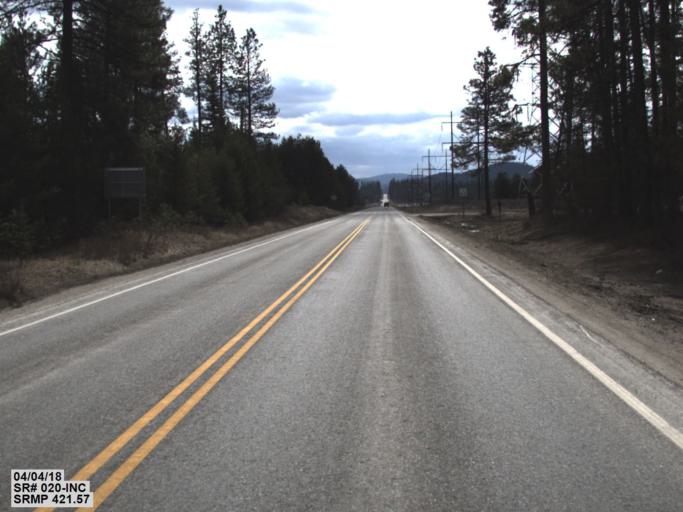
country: US
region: Washington
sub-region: Pend Oreille County
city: Newport
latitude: 48.3040
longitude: -117.2831
